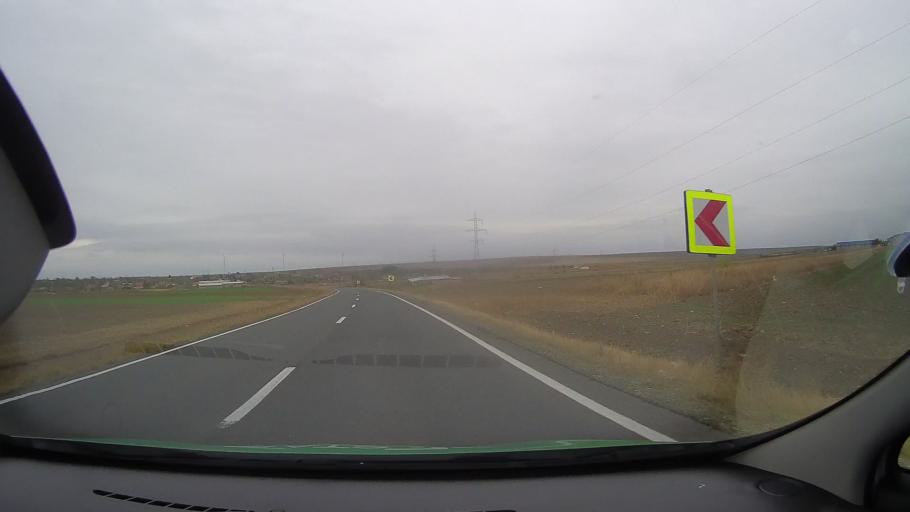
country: RO
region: Constanta
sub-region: Comuna Nicolae Balcescu
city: Dorobantu
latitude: 44.4159
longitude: 28.3158
